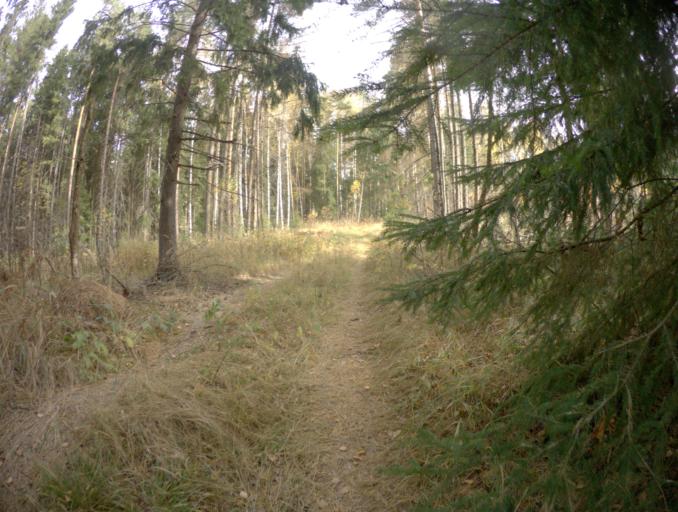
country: RU
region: Vladimir
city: Vorsha
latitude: 55.9554
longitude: 40.1290
